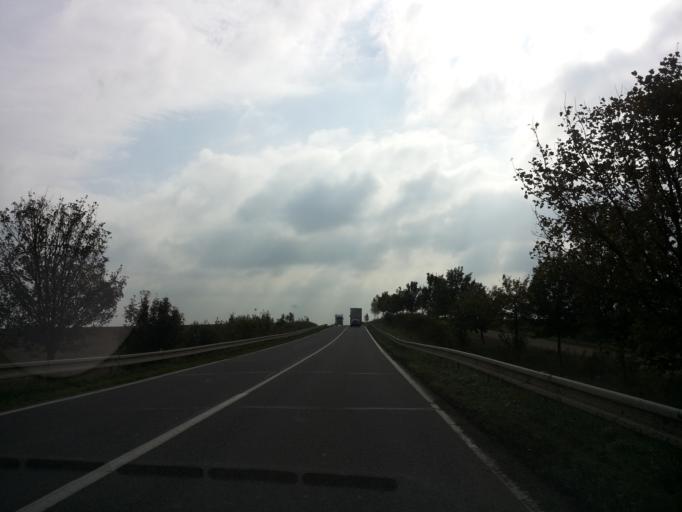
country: FR
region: Lorraine
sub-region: Departement de la Moselle
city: Solgne
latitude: 48.9813
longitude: 6.2887
